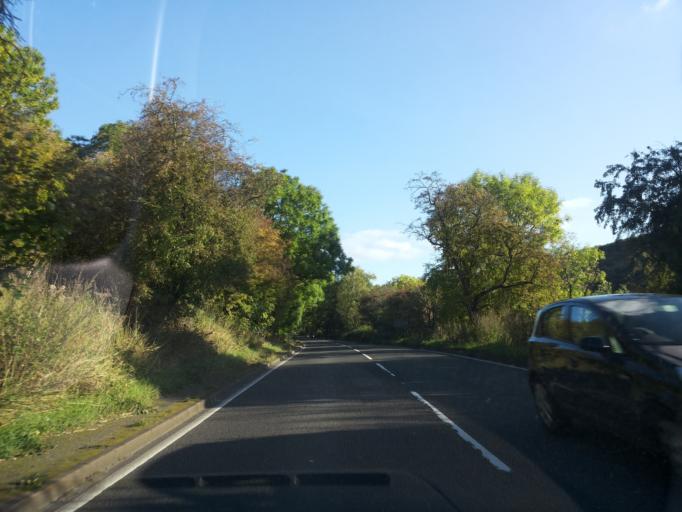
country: GB
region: England
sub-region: Derbyshire
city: Bakewell
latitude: 53.2443
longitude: -1.5806
